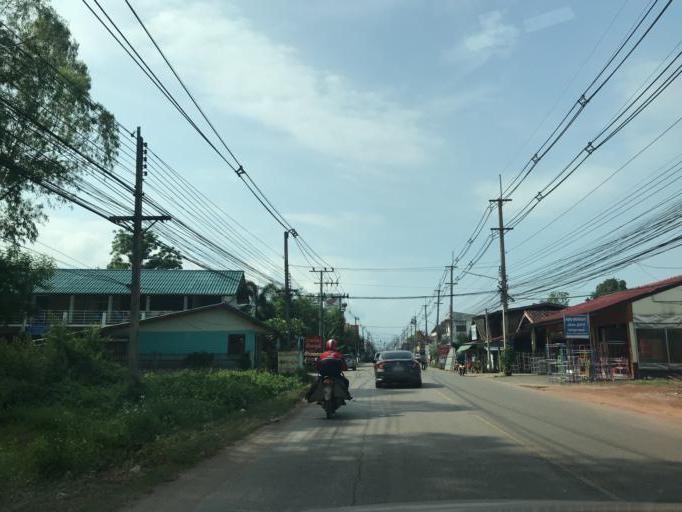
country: TH
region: Phayao
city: Chiang Kham
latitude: 19.5328
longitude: 100.3007
